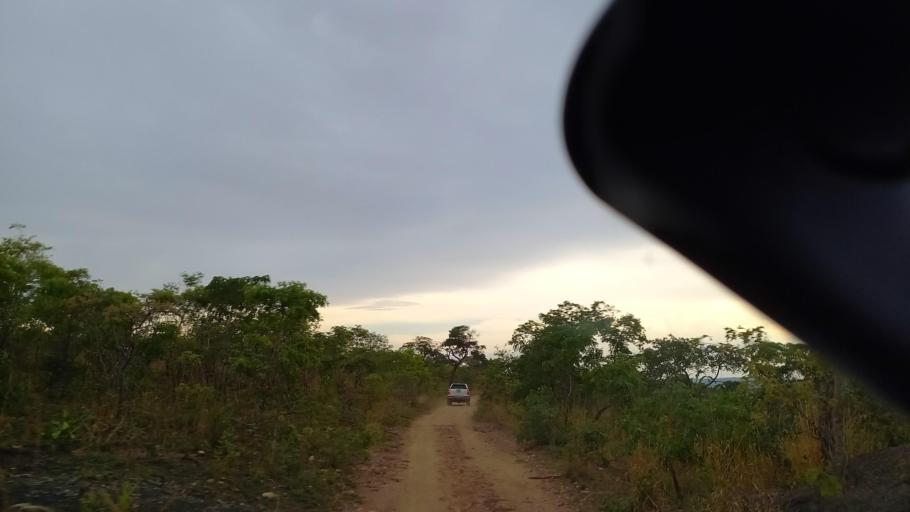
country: ZM
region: Lusaka
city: Kafue
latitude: -16.0512
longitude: 28.3355
